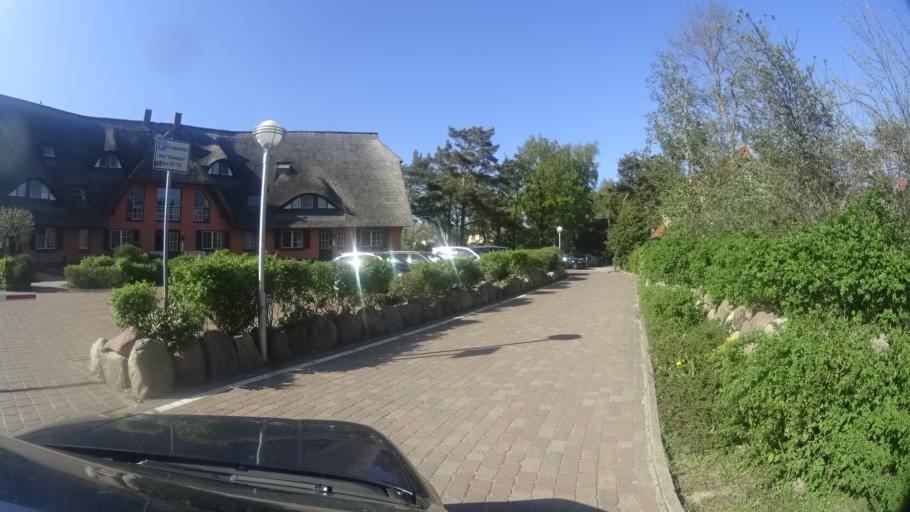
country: DE
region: Mecklenburg-Vorpommern
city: Ostseebad Dierhagen
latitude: 54.2831
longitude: 12.3146
